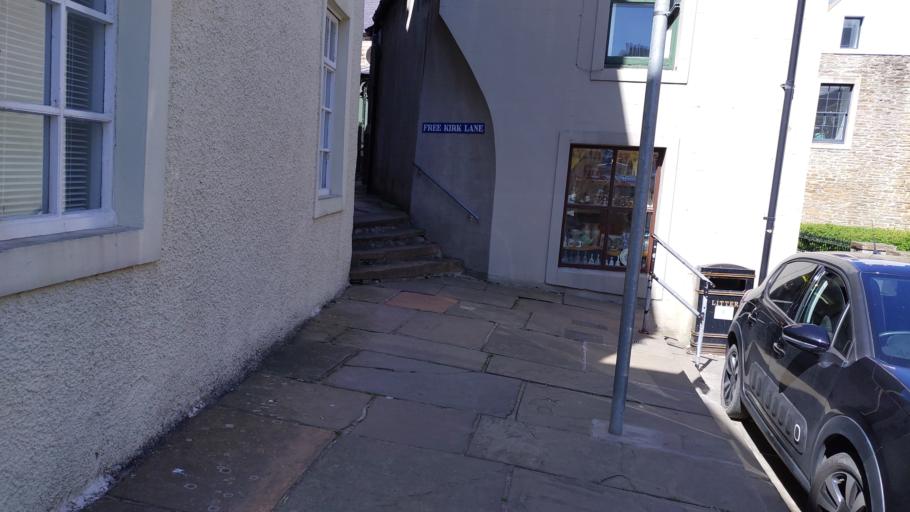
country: GB
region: Scotland
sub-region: Orkney Islands
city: Stromness
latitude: 58.9618
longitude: -3.2994
